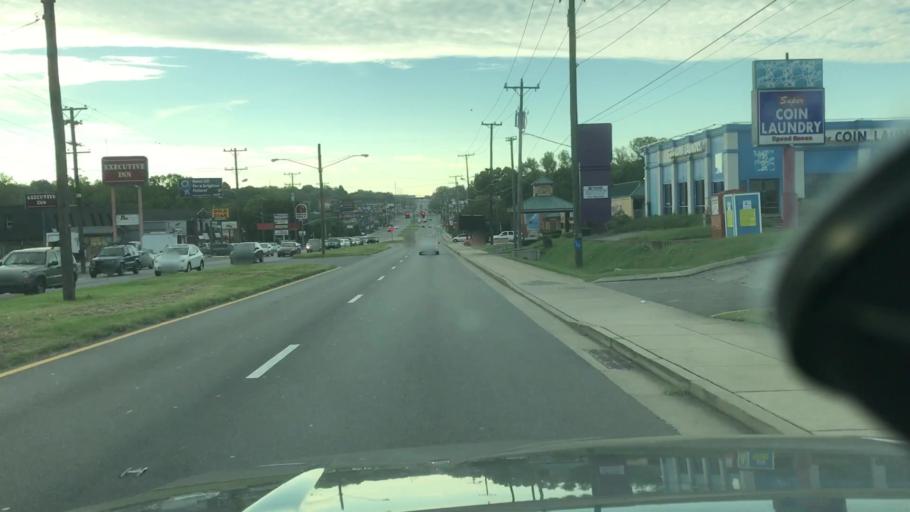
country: US
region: Tennessee
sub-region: Davidson County
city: Nashville
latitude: 36.1306
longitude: -86.7163
